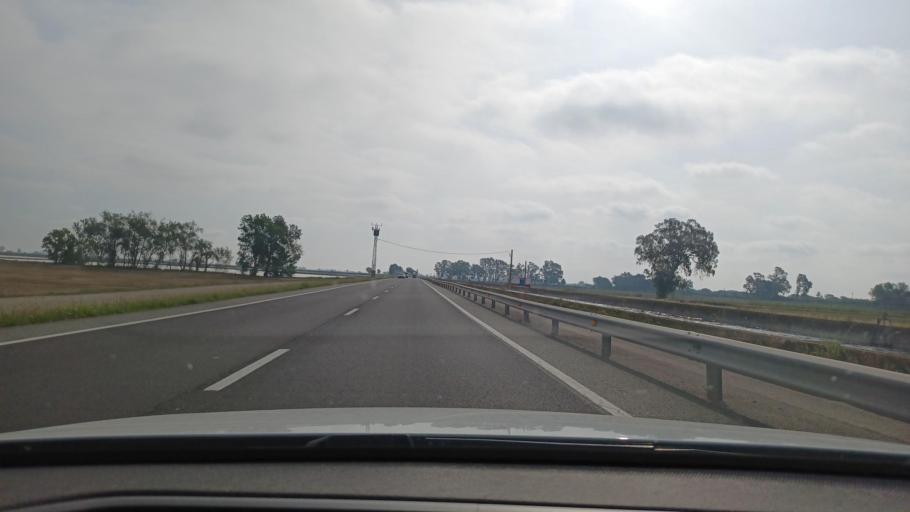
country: ES
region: Catalonia
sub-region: Provincia de Tarragona
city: Deltebre
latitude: 40.7194
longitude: 0.6458
